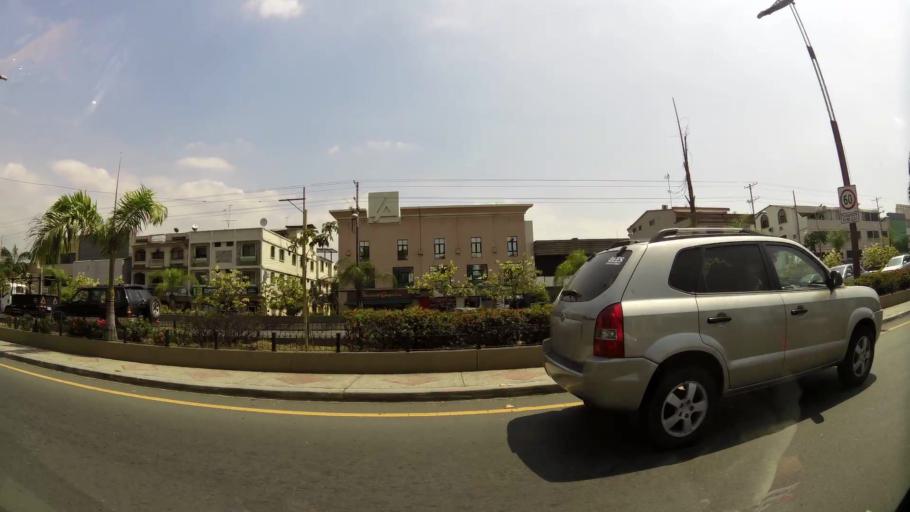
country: EC
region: Guayas
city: Eloy Alfaro
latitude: -2.1475
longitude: -79.8641
